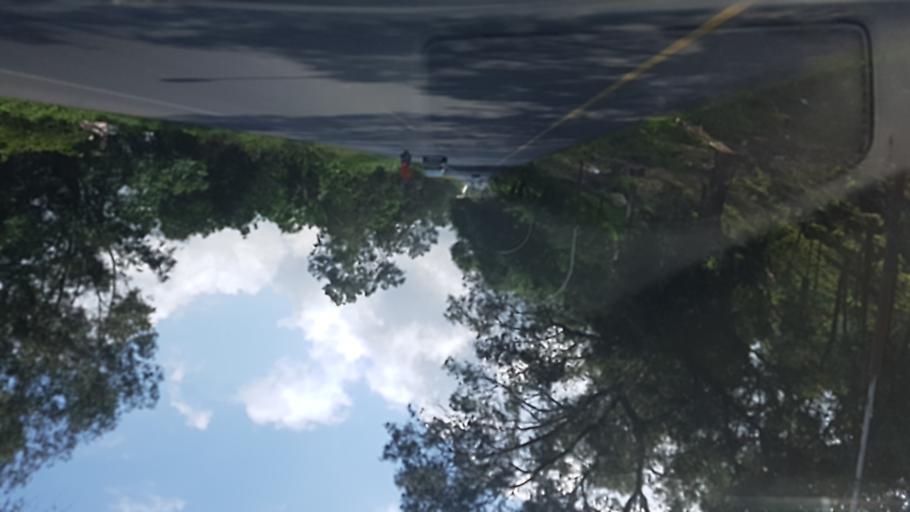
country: MX
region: Nayarit
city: Tepic
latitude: 21.4917
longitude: -104.9041
